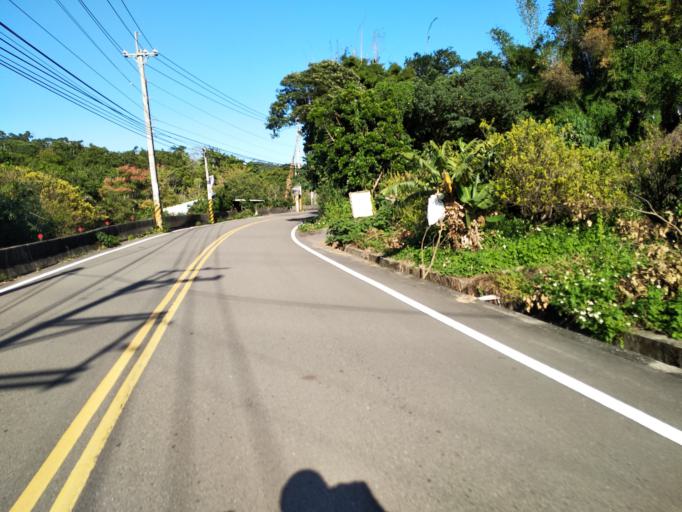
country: TW
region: Taiwan
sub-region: Hsinchu
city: Zhubei
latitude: 24.8554
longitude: 121.0908
